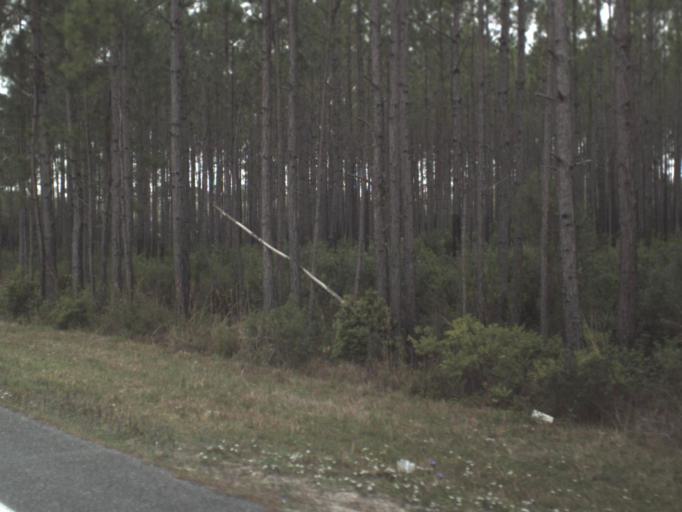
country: US
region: Florida
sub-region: Franklin County
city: Eastpoint
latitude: 29.7938
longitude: -84.8307
